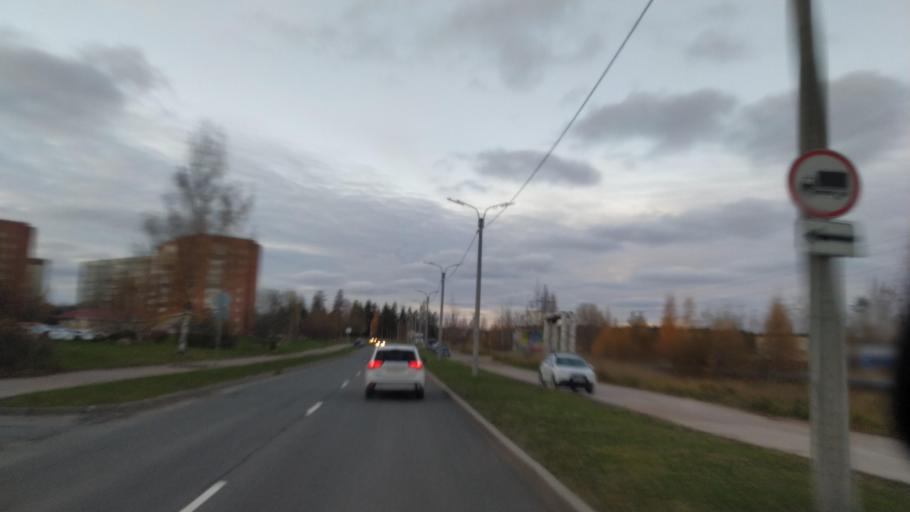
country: RU
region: Leningrad
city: Sosnovyy Bor
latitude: 59.9154
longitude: 29.0937
